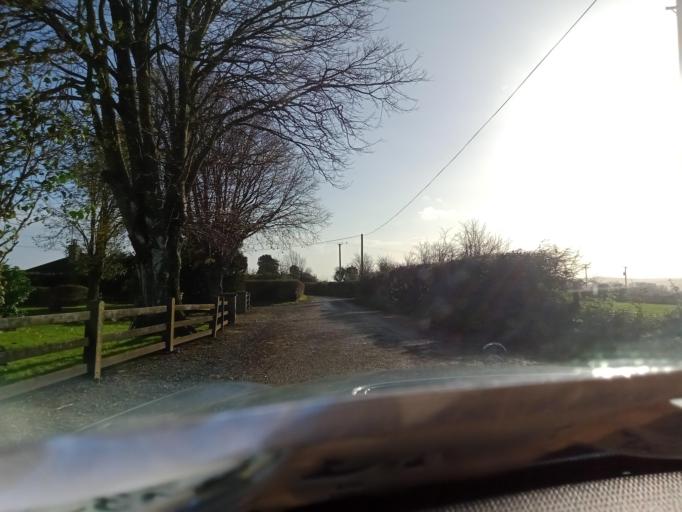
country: IE
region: Munster
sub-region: Waterford
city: Portlaw
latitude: 52.3211
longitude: -7.2856
